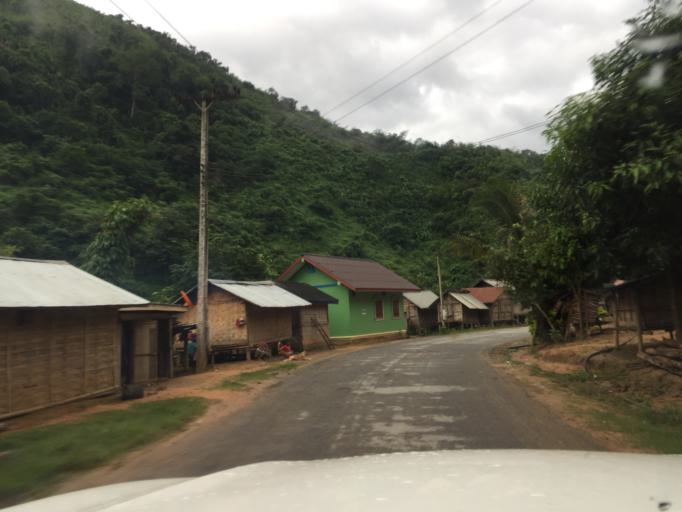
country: LA
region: Oudomxai
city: Muang La
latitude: 20.9870
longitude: 102.2274
